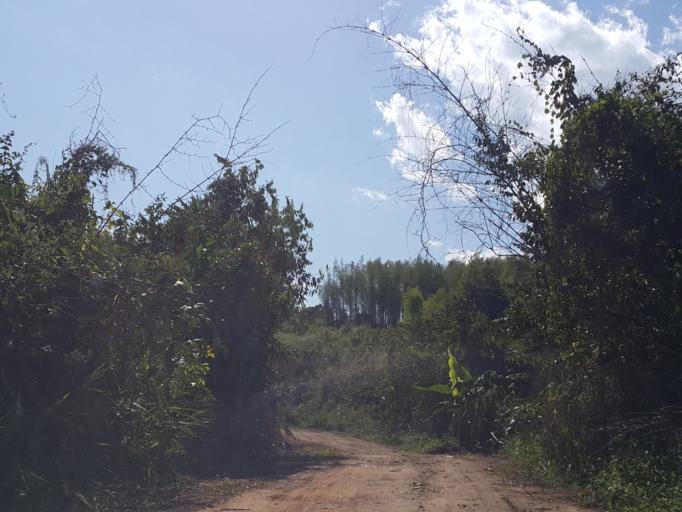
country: TH
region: Chiang Mai
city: Mae Taeng
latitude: 18.9585
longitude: 98.9025
